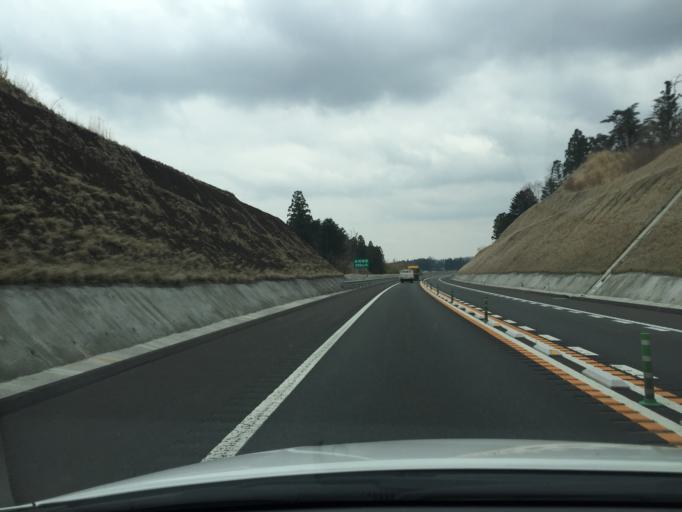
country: JP
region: Miyagi
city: Marumori
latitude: 37.8104
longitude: 140.8822
